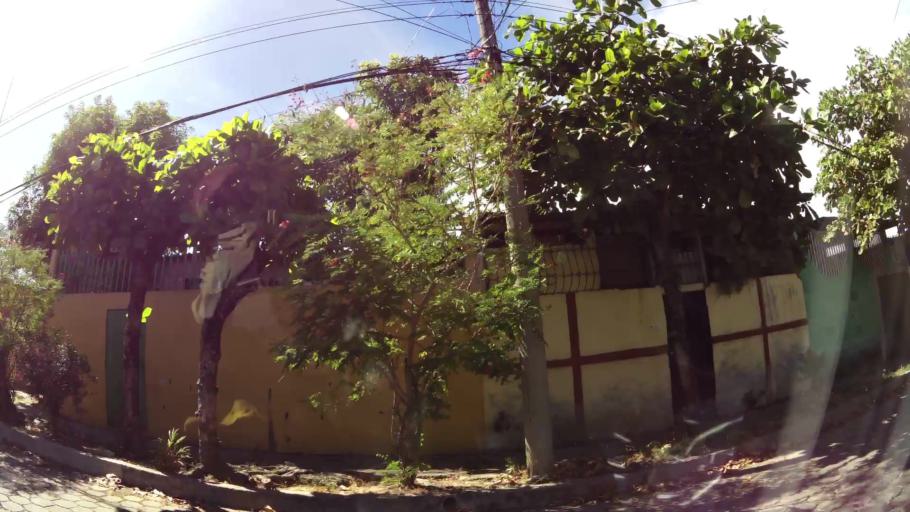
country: SV
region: San Salvador
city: Apopa
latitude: 13.8095
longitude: -89.1814
